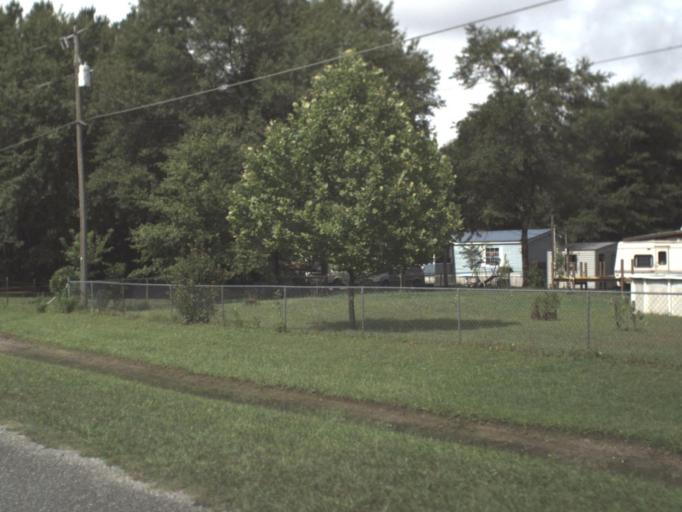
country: US
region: Florida
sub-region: Columbia County
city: Five Points
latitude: 30.2596
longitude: -82.6377
